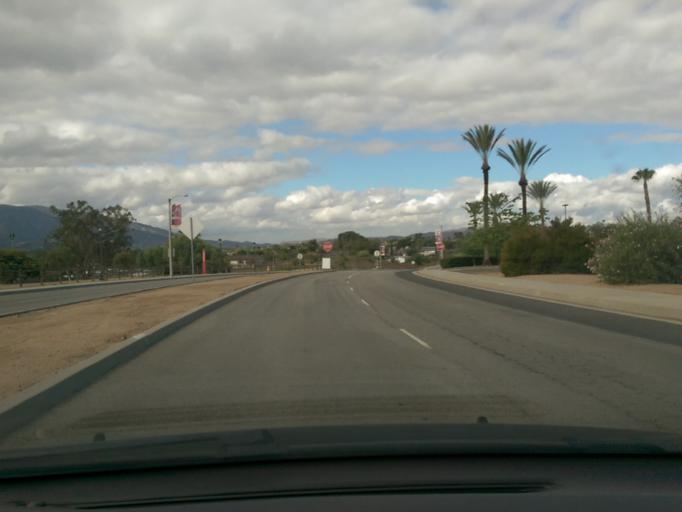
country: US
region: California
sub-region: Riverside County
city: Norco
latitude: 33.9156
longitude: -117.5671
